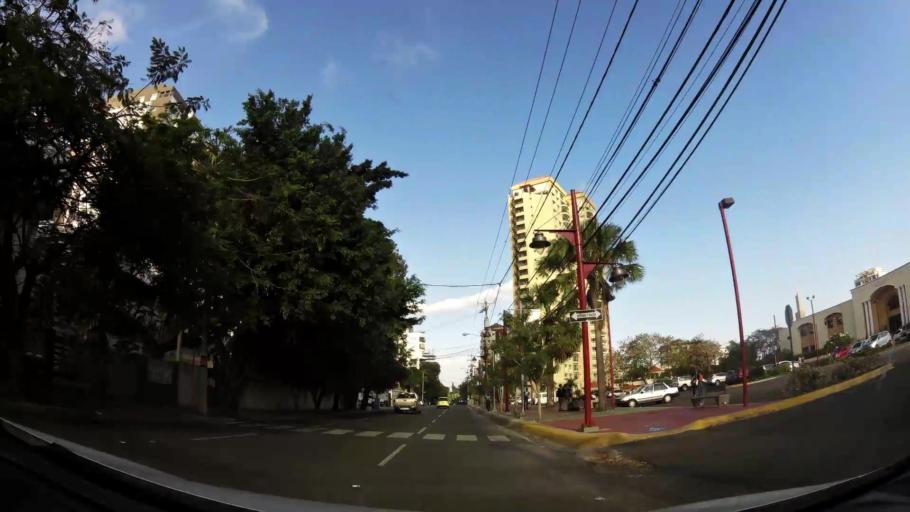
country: DO
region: Nacional
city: La Julia
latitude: 18.4683
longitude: -69.9188
